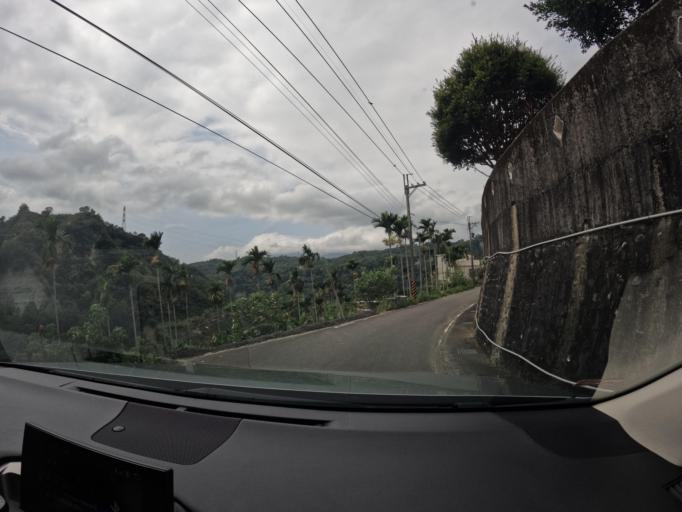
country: TW
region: Taiwan
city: Fengyuan
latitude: 24.3491
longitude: 120.8731
